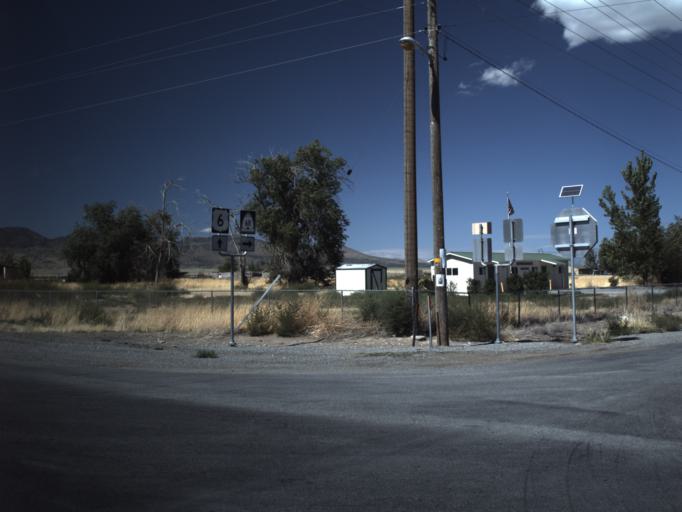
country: US
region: Utah
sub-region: Utah County
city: Genola
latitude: 39.9519
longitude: -111.9562
